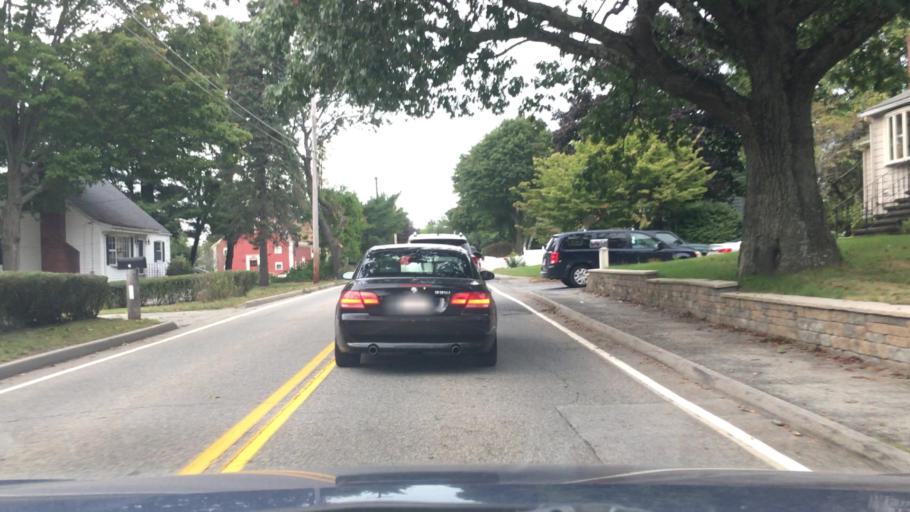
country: US
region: Massachusetts
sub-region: Middlesex County
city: Billerica
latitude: 42.5390
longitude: -71.2536
